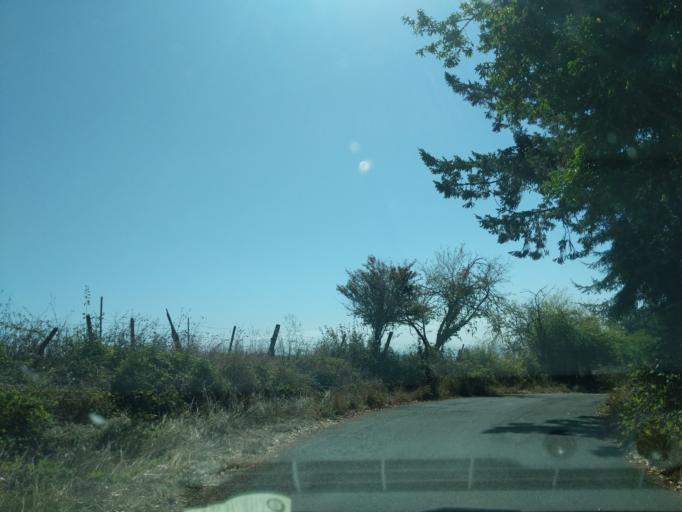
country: US
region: California
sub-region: Sonoma County
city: Monte Rio
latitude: 38.5224
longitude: -123.2417
